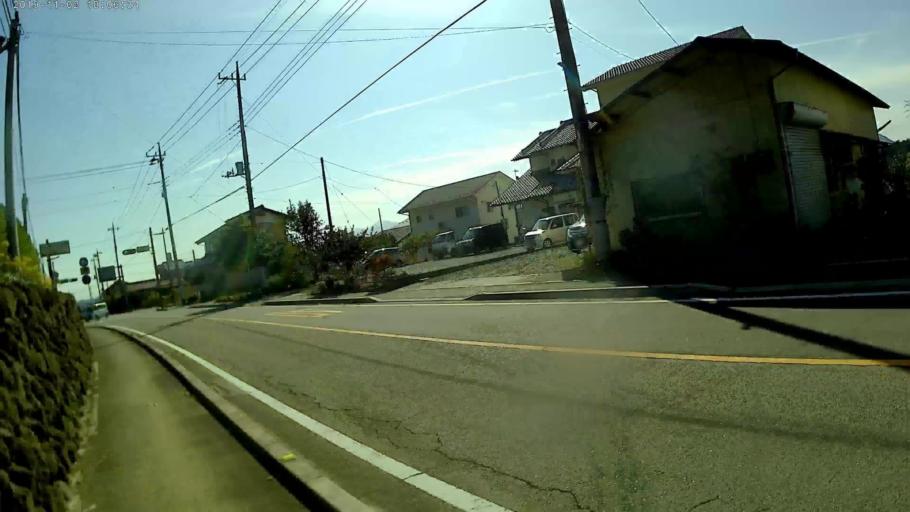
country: JP
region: Gunma
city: Annaka
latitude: 36.3186
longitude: 138.7878
